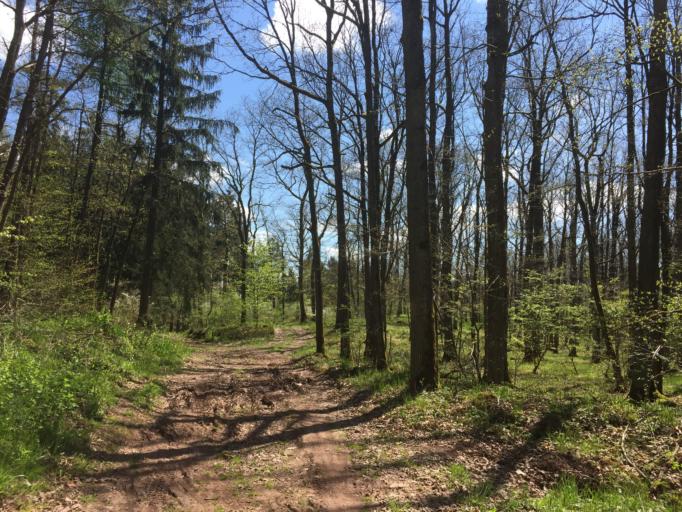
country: DE
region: Bavaria
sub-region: Regierungsbezirk Unterfranken
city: Bad Konigshofen im Grabfeld
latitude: 50.2532
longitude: 10.4546
